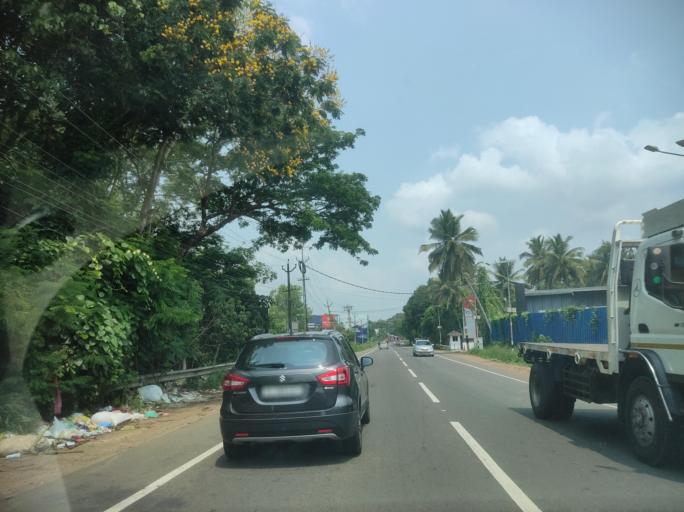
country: IN
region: Kerala
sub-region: Kottayam
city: Changanacheri
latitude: 9.4146
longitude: 76.5522
